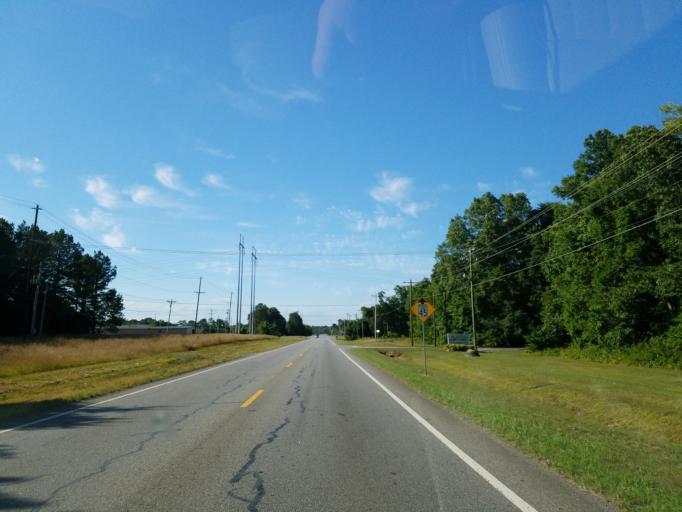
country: US
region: Georgia
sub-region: Gordon County
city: Calhoun
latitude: 34.4673
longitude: -84.9344
